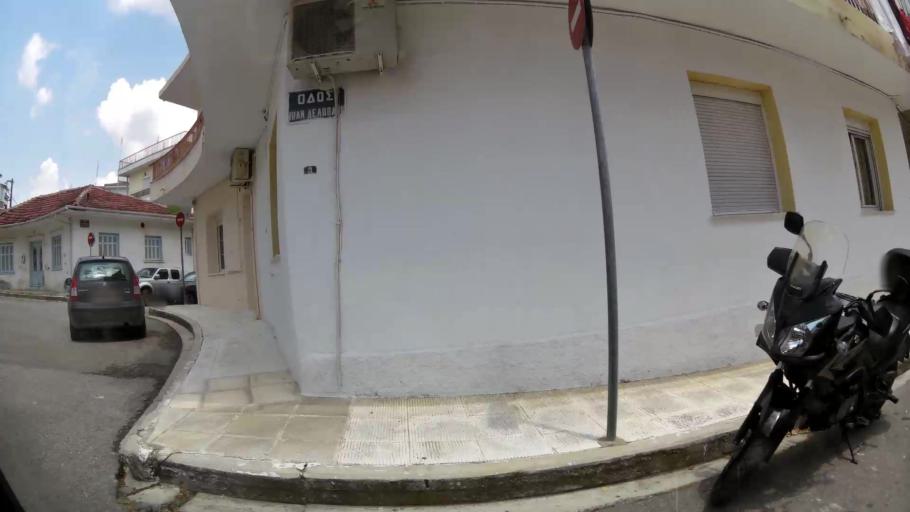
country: GR
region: West Macedonia
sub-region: Nomos Kozanis
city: Kozani
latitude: 40.2955
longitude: 21.7842
